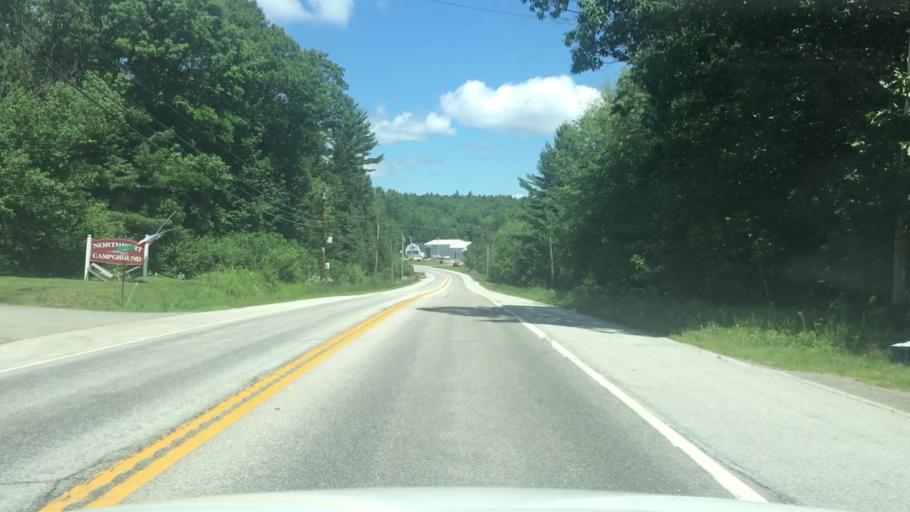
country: US
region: Maine
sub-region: Waldo County
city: Northport
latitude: 44.3509
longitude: -68.9683
